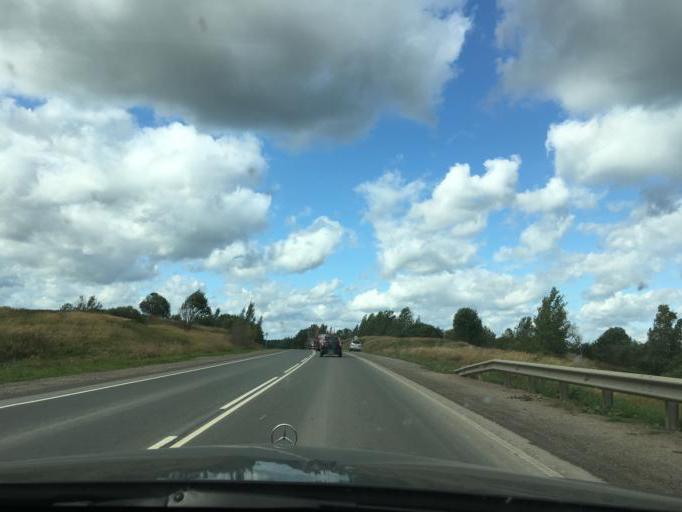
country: RU
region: Pskov
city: Novosokol'niki
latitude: 56.2991
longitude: 30.2206
